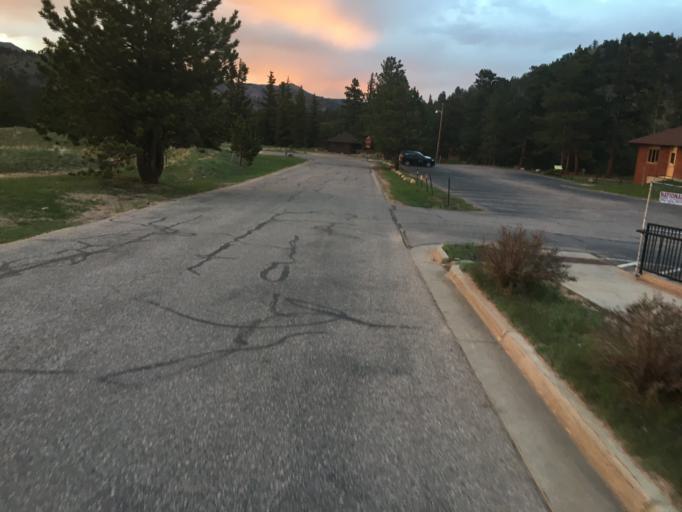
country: US
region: Colorado
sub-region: Larimer County
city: Estes Park
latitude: 40.3415
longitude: -105.5706
